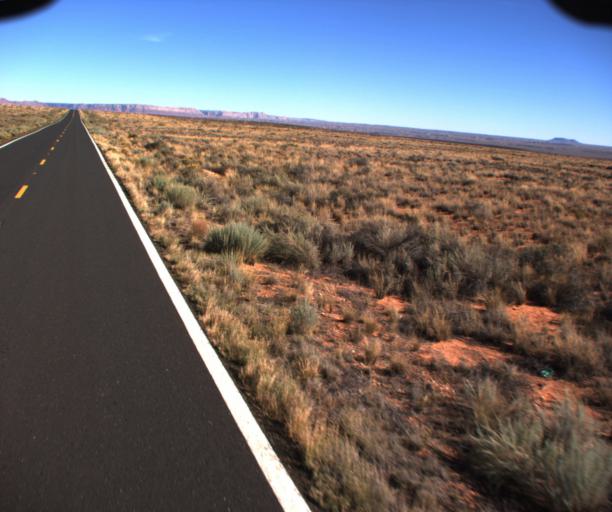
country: US
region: Arizona
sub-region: Coconino County
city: Page
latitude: 36.6951
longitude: -111.9049
